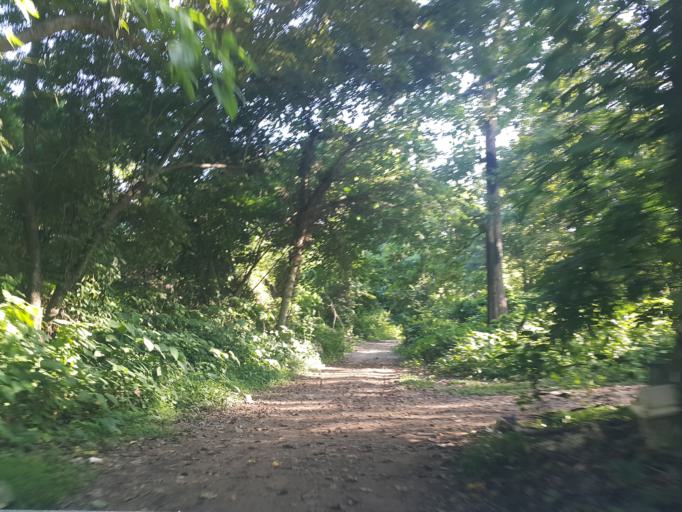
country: TH
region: Chiang Mai
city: Mae On
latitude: 18.7075
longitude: 99.2033
